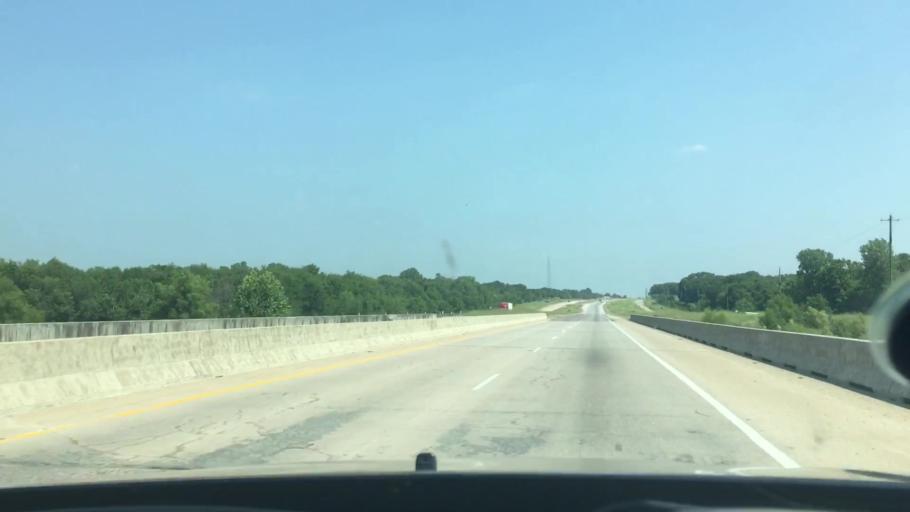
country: US
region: Oklahoma
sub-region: Atoka County
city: Atoka
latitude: 34.2589
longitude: -96.2115
